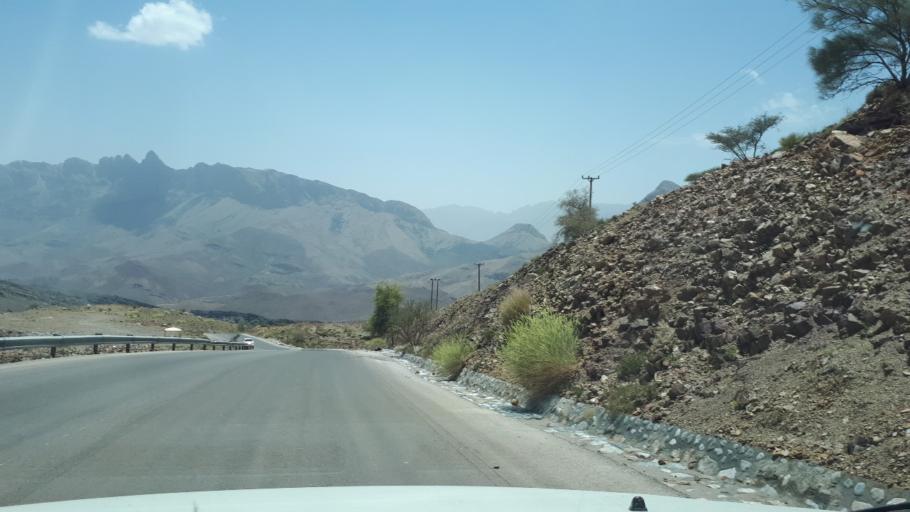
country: OM
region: Muhafazat ad Dakhiliyah
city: Bahla'
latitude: 23.2096
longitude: 57.1470
